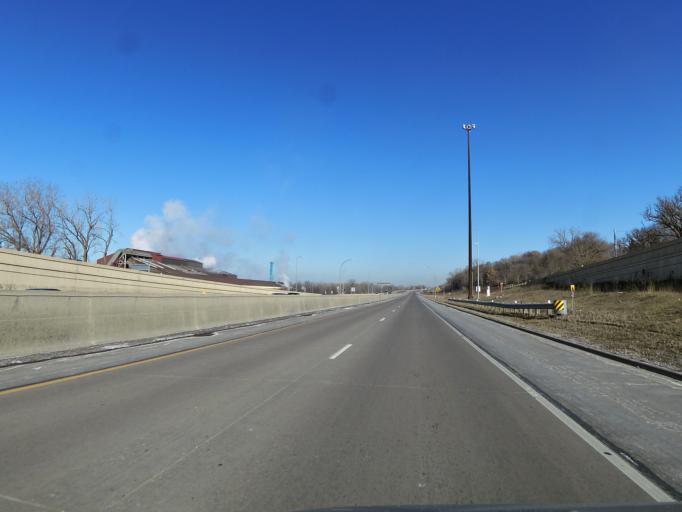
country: US
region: Minnesota
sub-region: Dakota County
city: South Saint Paul
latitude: 44.8931
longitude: -93.0075
